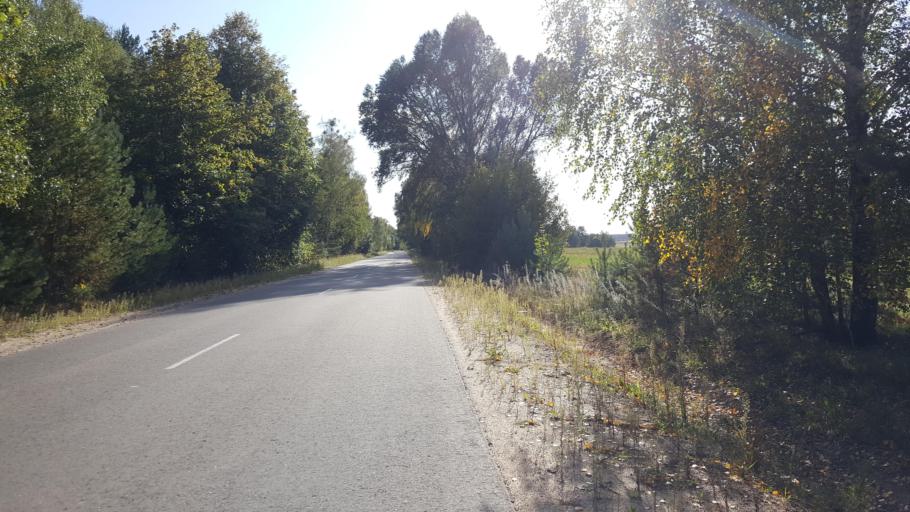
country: BY
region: Brest
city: Kamyanyets
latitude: 52.4042
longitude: 23.9060
